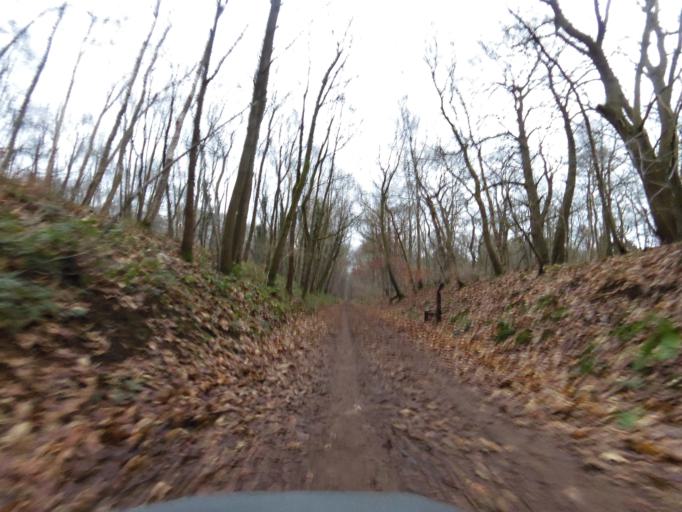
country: GB
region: England
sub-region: Norfolk
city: Costessey
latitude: 52.7075
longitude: 1.1779
